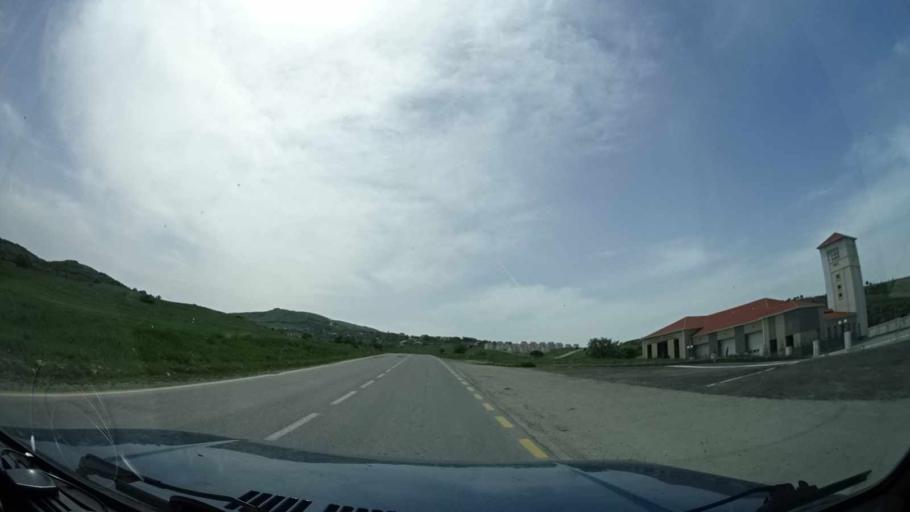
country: AZ
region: Xizi
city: Khyzy
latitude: 40.9072
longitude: 49.0931
